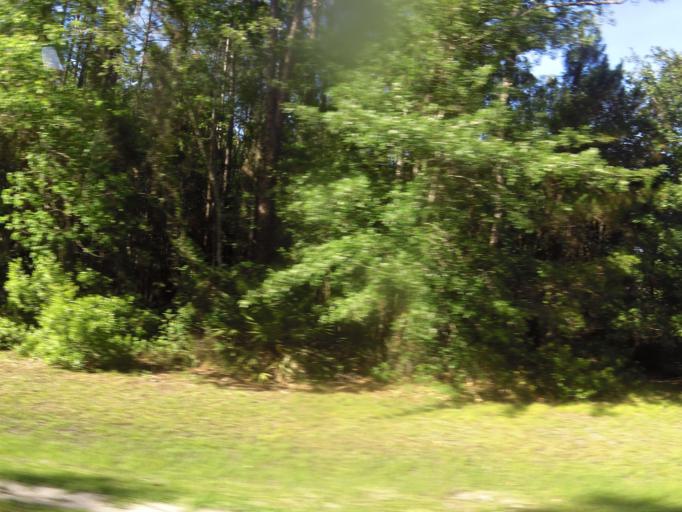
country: US
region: Florida
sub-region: Nassau County
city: Callahan
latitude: 30.5564
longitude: -81.7912
